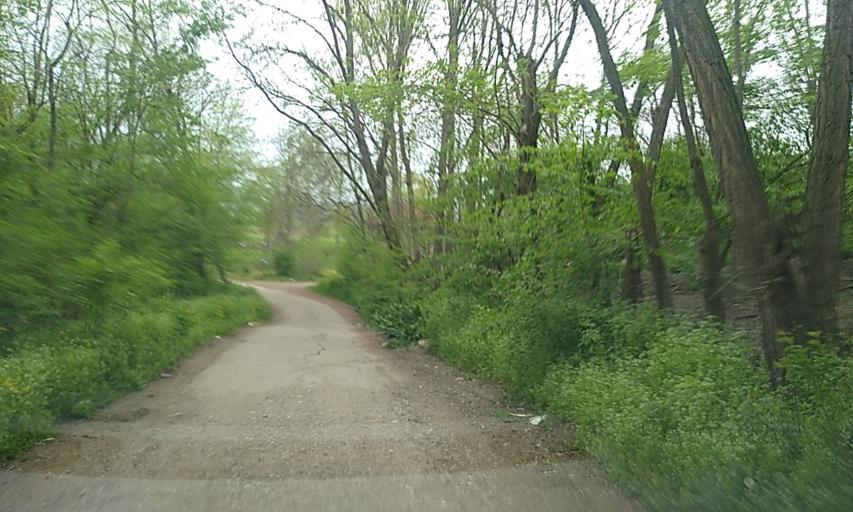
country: RS
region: Central Serbia
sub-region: Nisavski Okrug
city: Razanj
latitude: 43.5969
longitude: 21.6172
